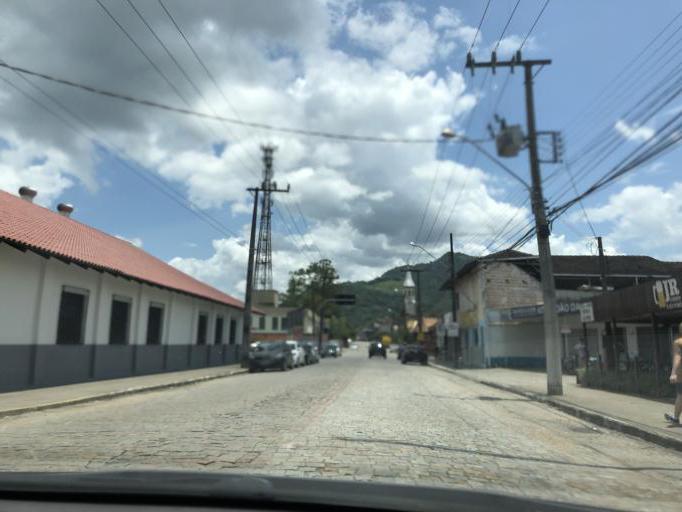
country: BR
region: Santa Catarina
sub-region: Jaragua Do Sul
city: Jaragua do Sul
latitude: -26.5142
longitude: -49.1275
